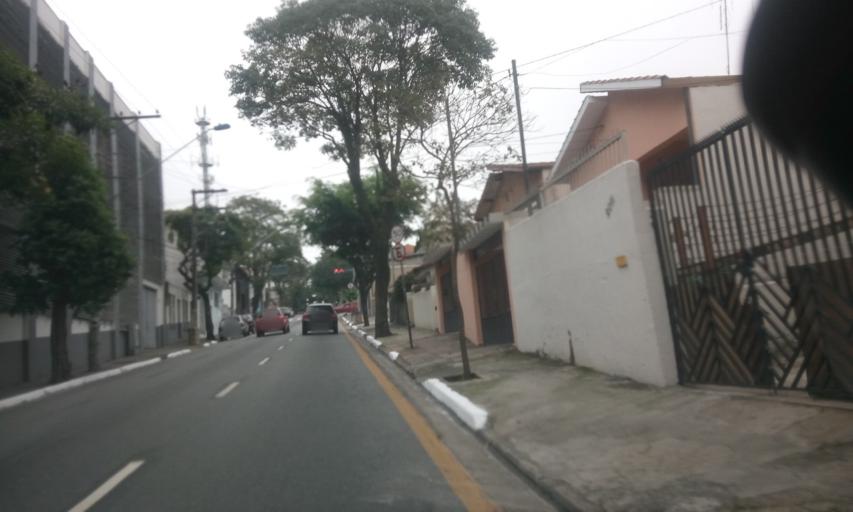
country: BR
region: Sao Paulo
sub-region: Sao Caetano Do Sul
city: Sao Caetano do Sul
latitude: -23.6289
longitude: -46.5693
